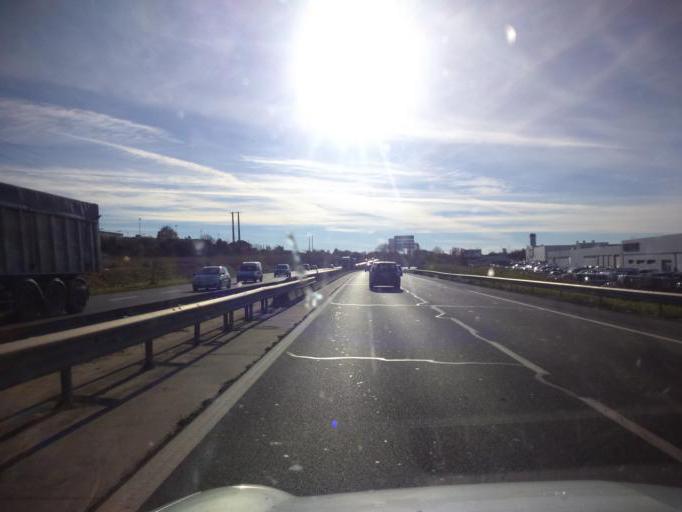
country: FR
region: Poitou-Charentes
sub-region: Departement de la Charente-Maritime
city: Perigny
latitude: 46.1565
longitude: -1.1171
